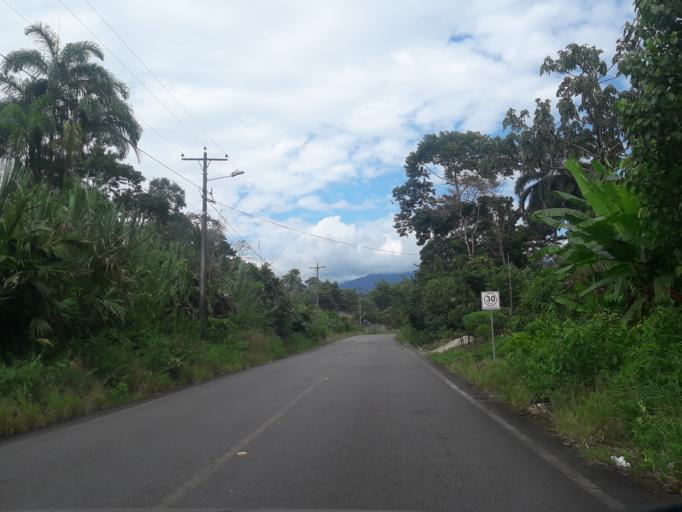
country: EC
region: Napo
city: Tena
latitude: -1.0383
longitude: -77.8933
